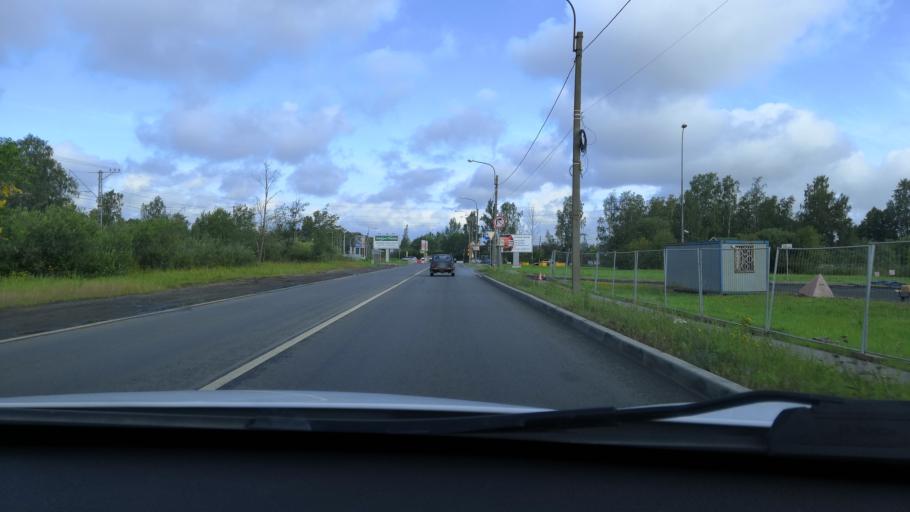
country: RU
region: St.-Petersburg
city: Tyarlevo
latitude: 59.7110
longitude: 30.4362
